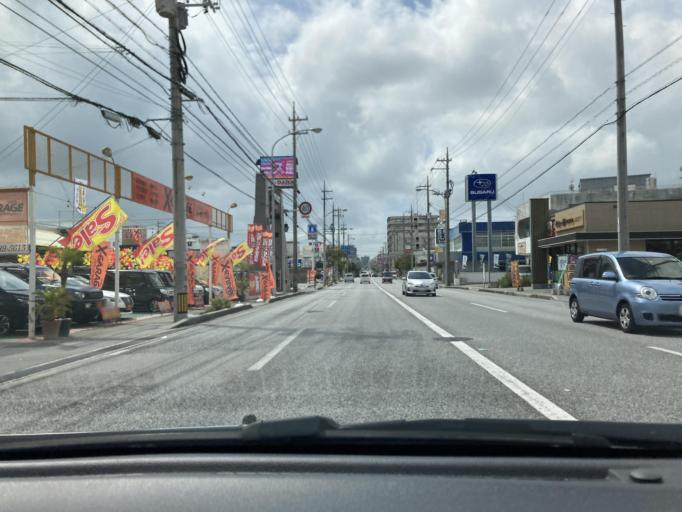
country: JP
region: Okinawa
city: Okinawa
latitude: 26.3508
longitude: 127.8268
